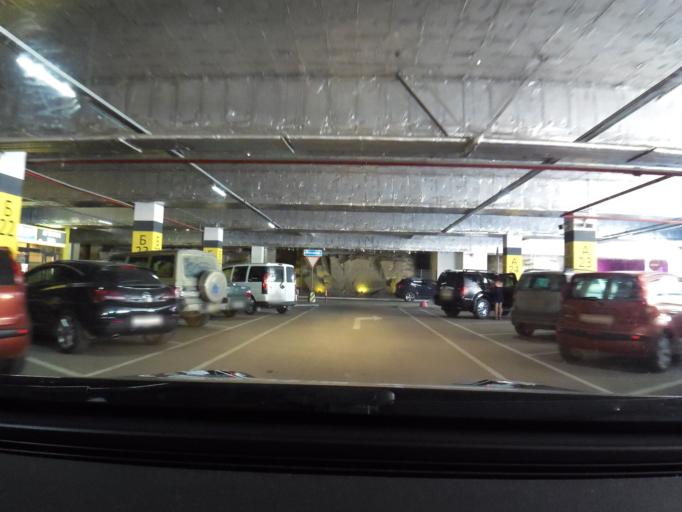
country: RU
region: Sverdlovsk
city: Shirokaya Rechka
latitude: 56.8185
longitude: 60.5365
